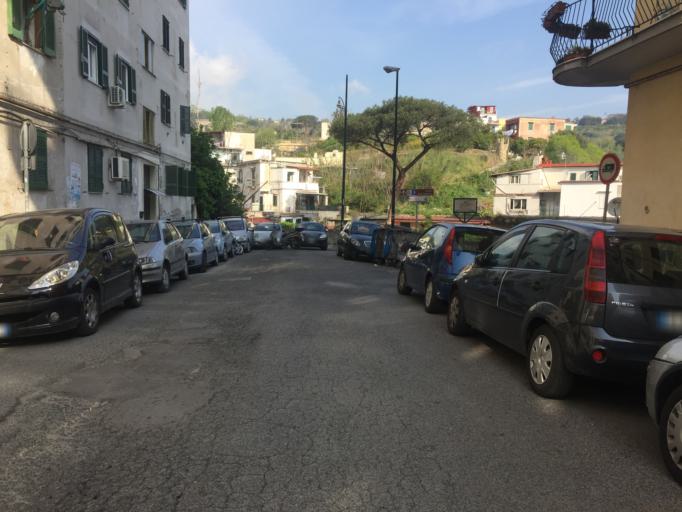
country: IT
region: Campania
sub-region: Provincia di Napoli
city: Napoli
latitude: 40.8582
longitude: 14.2415
